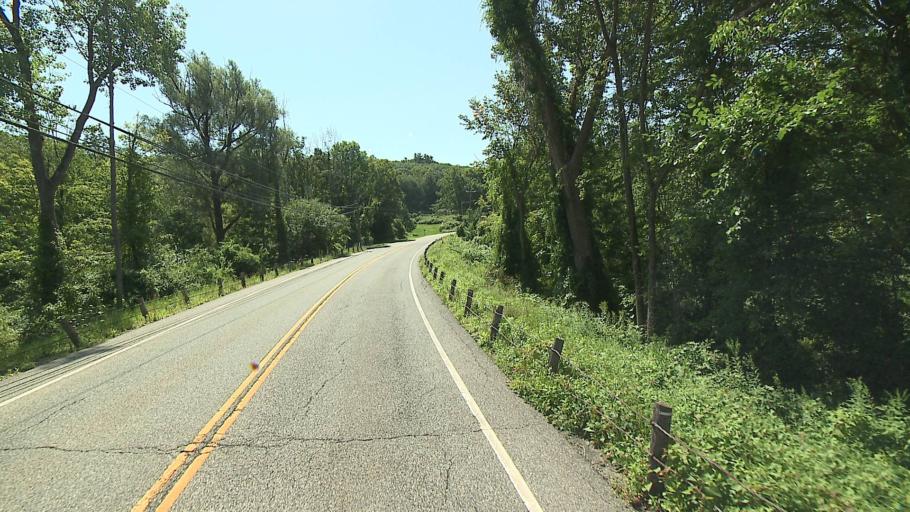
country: US
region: Connecticut
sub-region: Litchfield County
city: Kent
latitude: 41.8514
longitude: -73.4413
